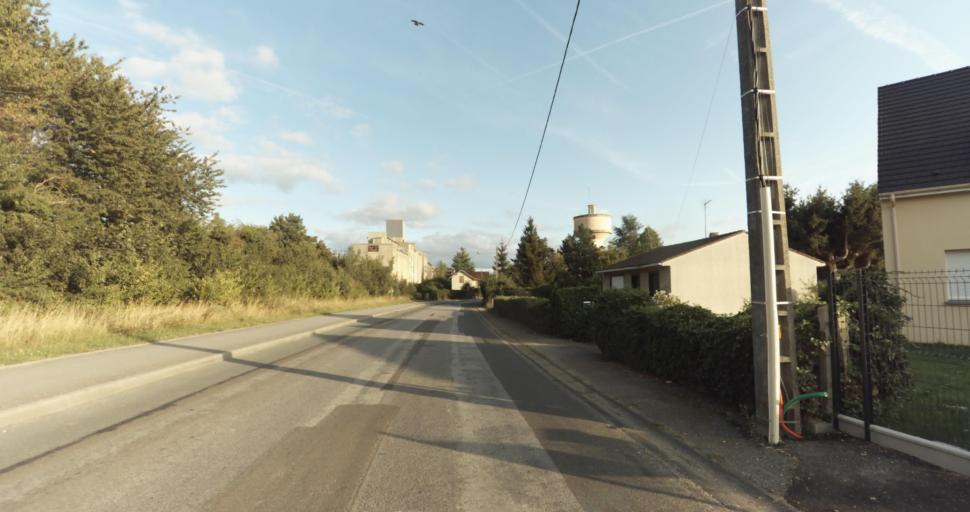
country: FR
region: Haute-Normandie
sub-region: Departement de l'Eure
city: Marcilly-sur-Eure
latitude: 48.9035
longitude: 1.2719
